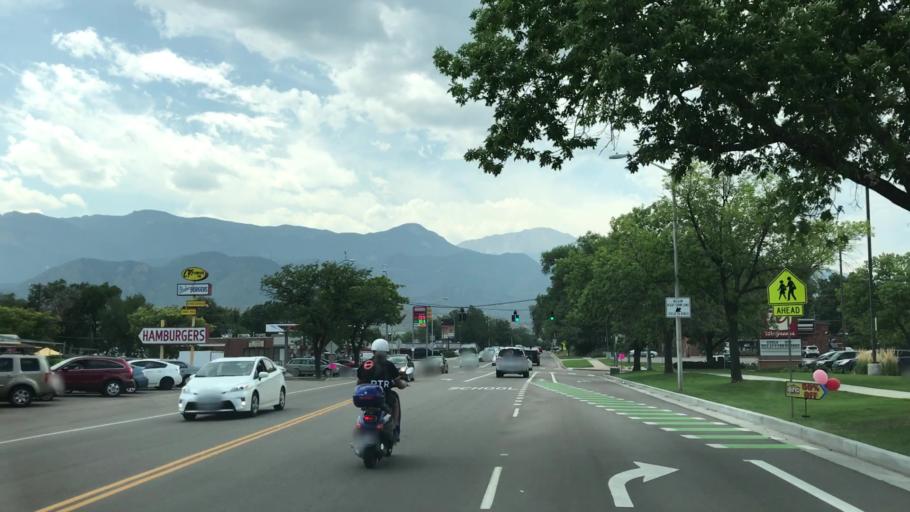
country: US
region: Colorado
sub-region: El Paso County
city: Colorado Springs
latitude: 38.8480
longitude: -104.8488
